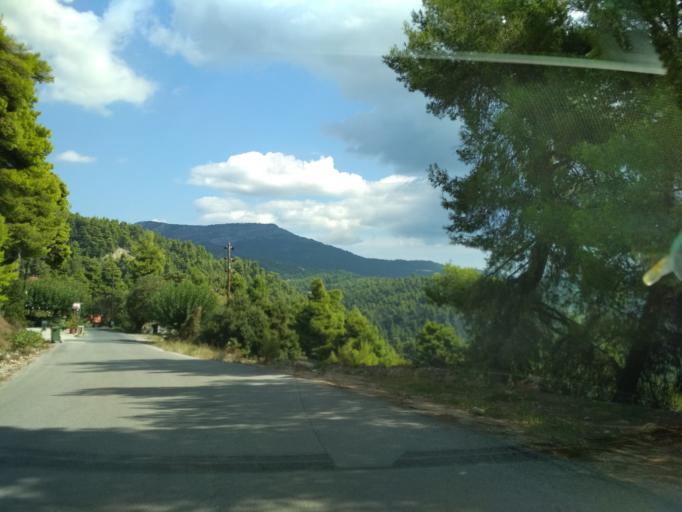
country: GR
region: Central Greece
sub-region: Nomos Evvoias
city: Roviai
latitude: 38.8252
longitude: 23.2800
